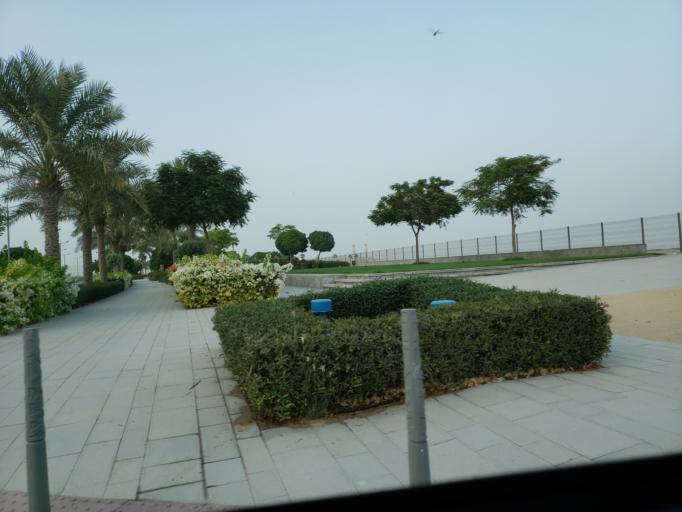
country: AE
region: Ajman
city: Ajman
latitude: 25.4366
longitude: 55.4661
